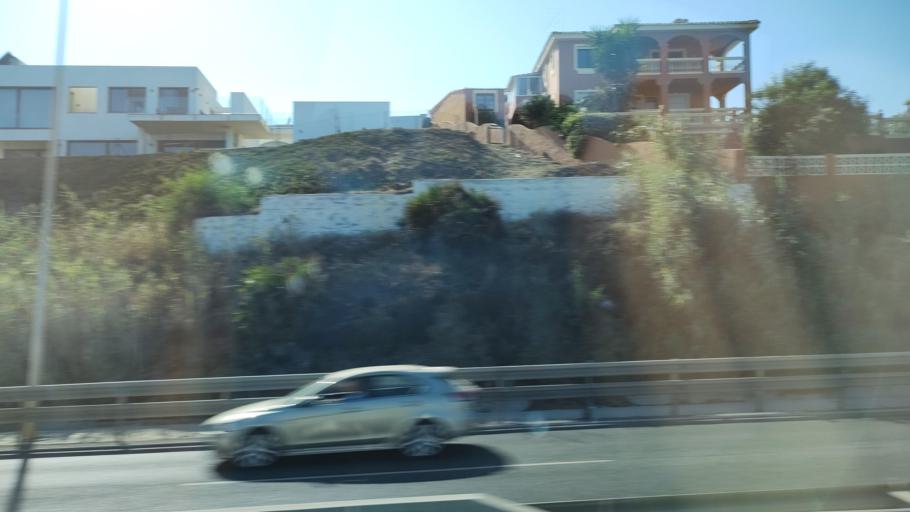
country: ES
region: Andalusia
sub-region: Provincia de Malaga
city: Fuengirola
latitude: 36.5102
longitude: -4.6362
